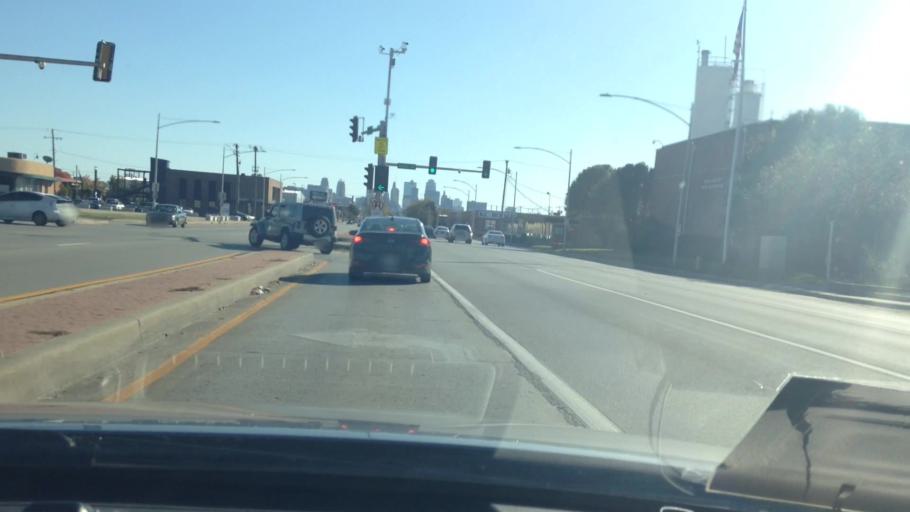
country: US
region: Missouri
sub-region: Clay County
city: North Kansas City
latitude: 39.1418
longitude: -94.5804
